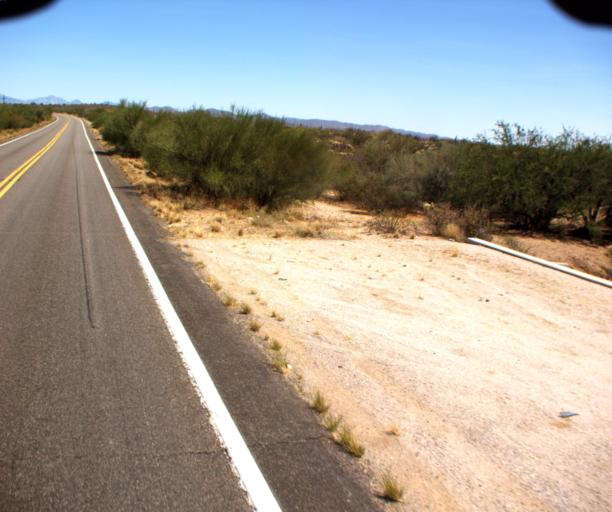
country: US
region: Arizona
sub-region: Pima County
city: Catalina
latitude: 32.7079
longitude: -111.0982
